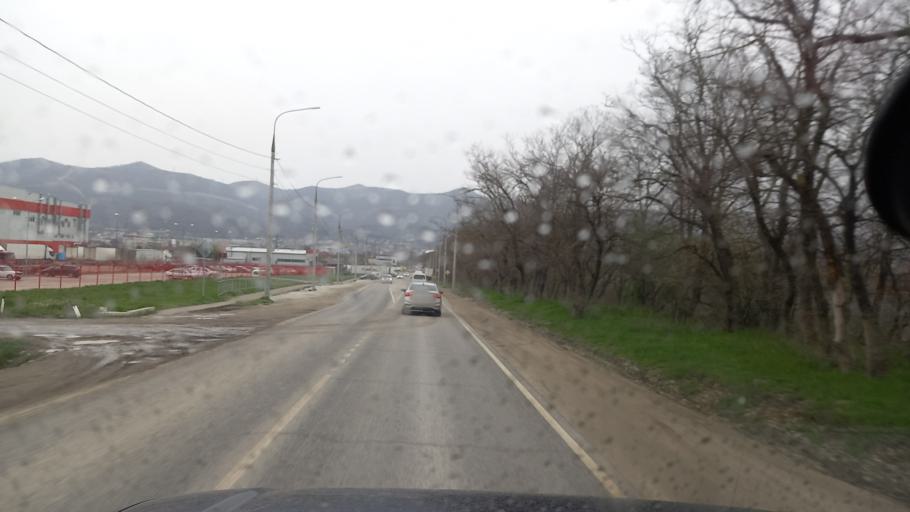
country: RU
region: Krasnodarskiy
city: Gayduk
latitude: 44.7568
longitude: 37.7076
